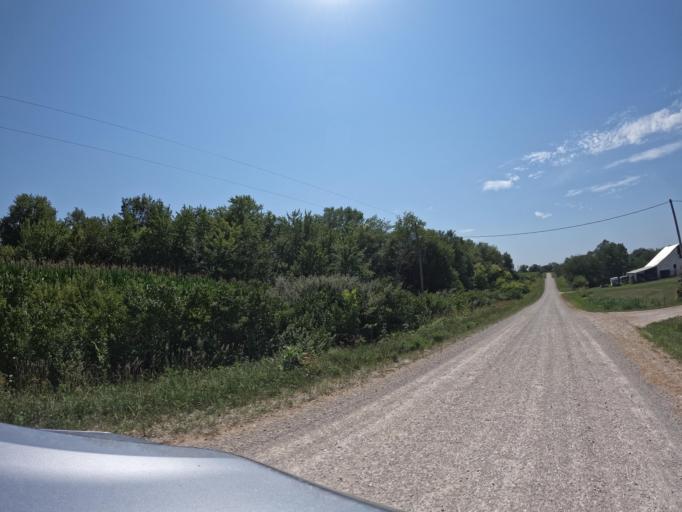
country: US
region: Iowa
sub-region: Henry County
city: Mount Pleasant
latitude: 40.8900
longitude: -91.6494
